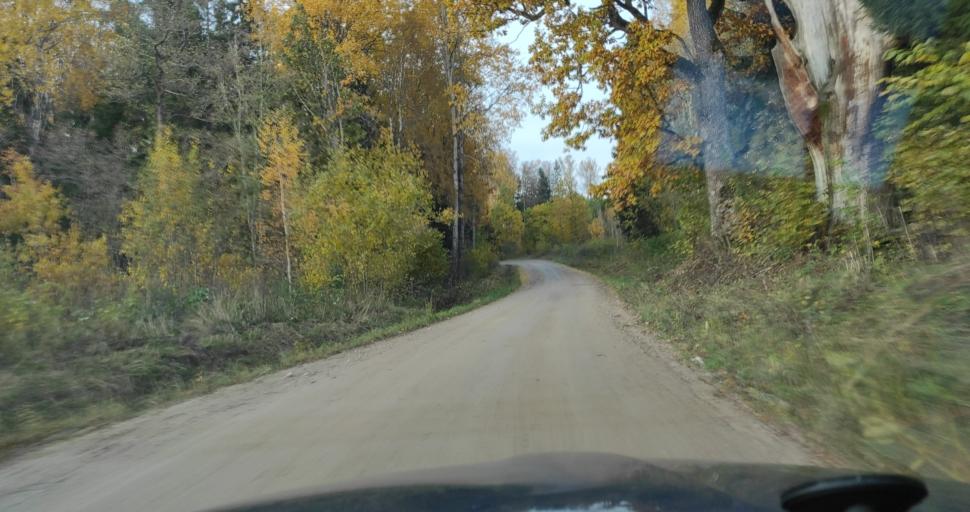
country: LV
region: Vainode
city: Vainode
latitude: 56.6295
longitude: 21.8168
